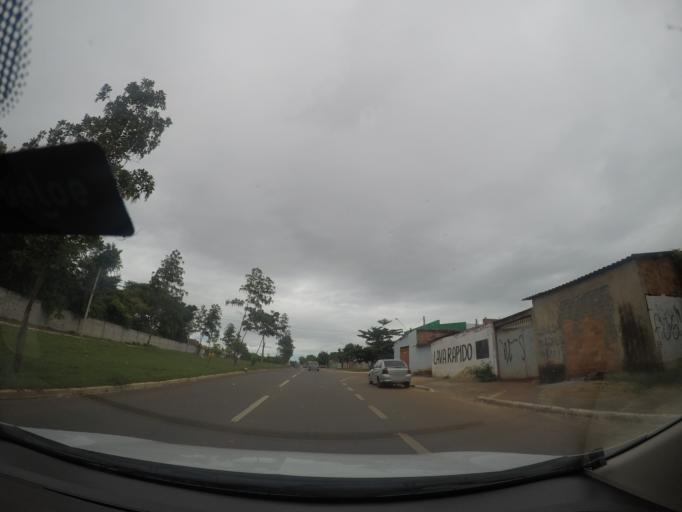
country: BR
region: Goias
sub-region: Goiania
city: Goiania
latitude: -16.6173
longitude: -49.3393
